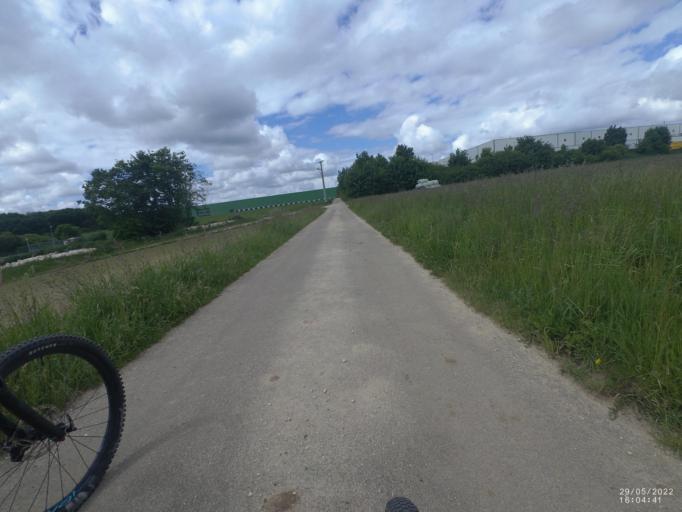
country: DE
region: Baden-Wuerttemberg
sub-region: Tuebingen Region
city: Setzingen
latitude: 48.5861
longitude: 10.1243
